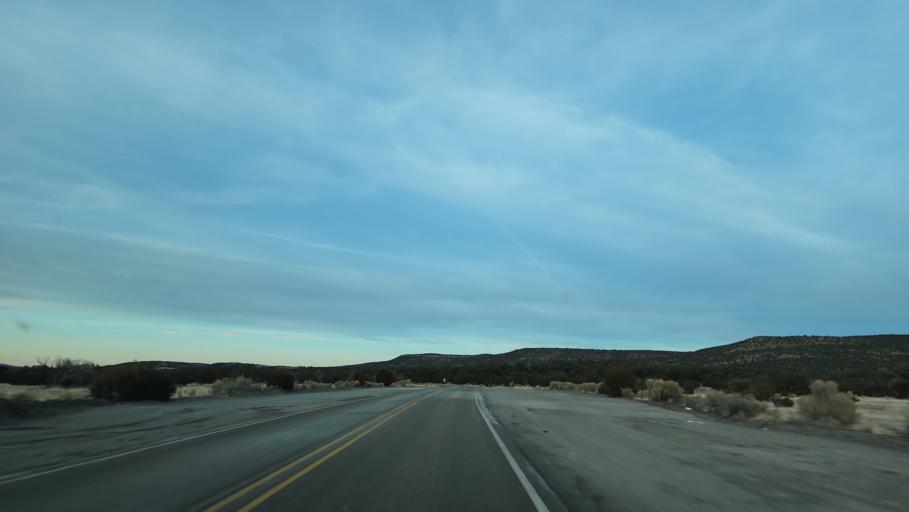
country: US
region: New Mexico
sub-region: Cibola County
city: Grants
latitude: 34.7237
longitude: -107.9769
